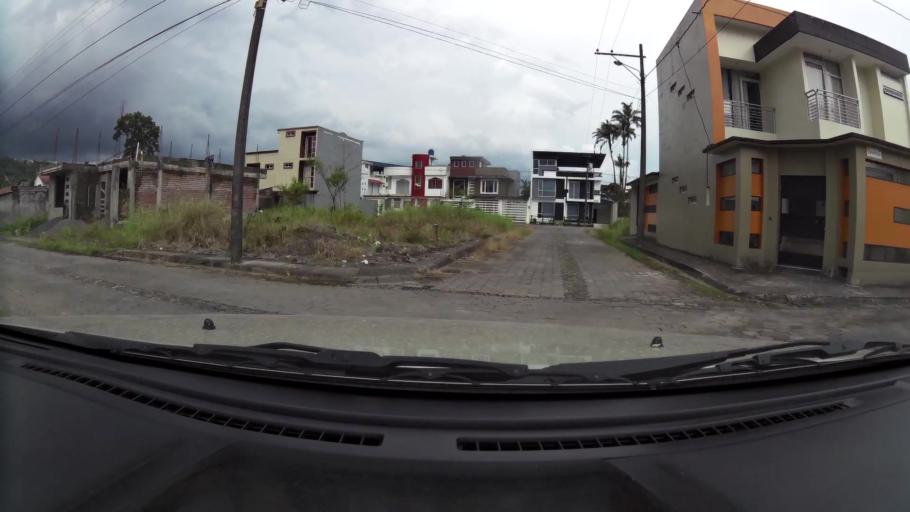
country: EC
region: Pastaza
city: Puyo
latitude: -1.4958
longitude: -78.0155
